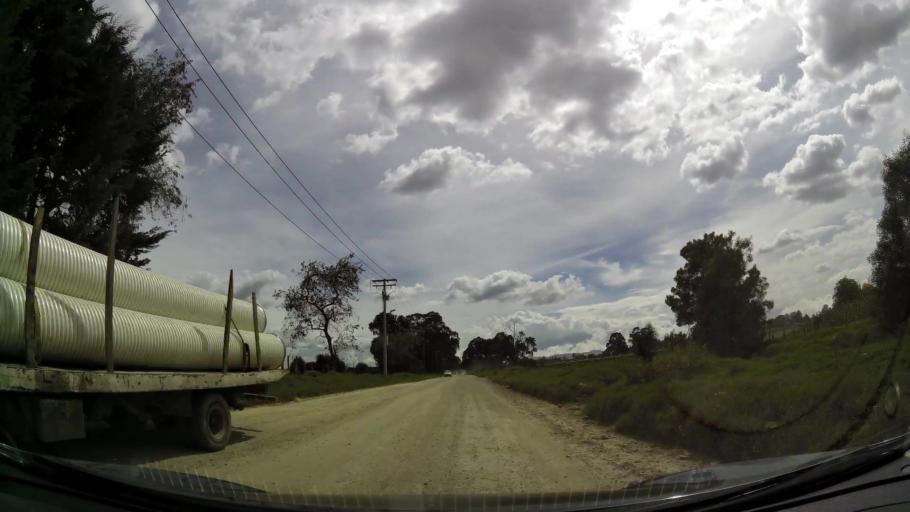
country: CO
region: Cundinamarca
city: Funza
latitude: 4.7236
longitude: -74.1643
